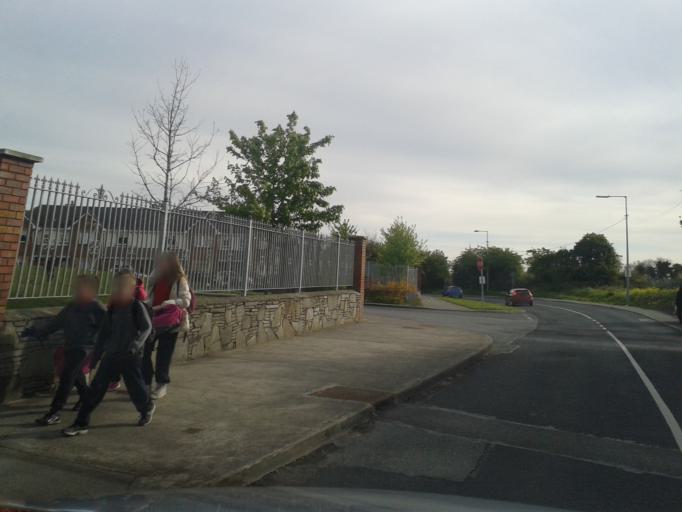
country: IE
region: Leinster
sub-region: Fingal County
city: Swords
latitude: 53.4484
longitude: -6.2332
